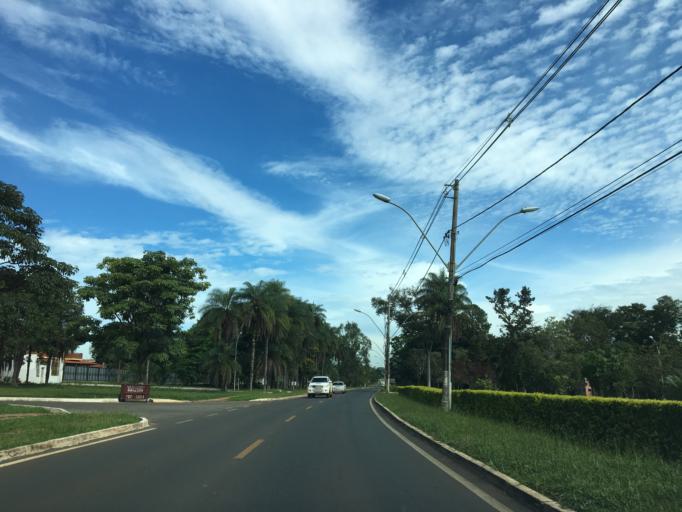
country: BR
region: Federal District
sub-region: Brasilia
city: Brasilia
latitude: -15.8638
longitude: -47.9741
